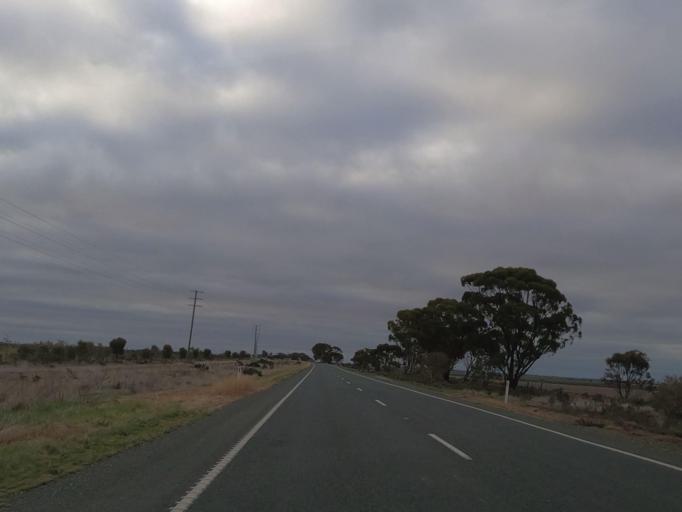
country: AU
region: Victoria
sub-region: Swan Hill
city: Swan Hill
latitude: -35.5776
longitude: 143.7884
